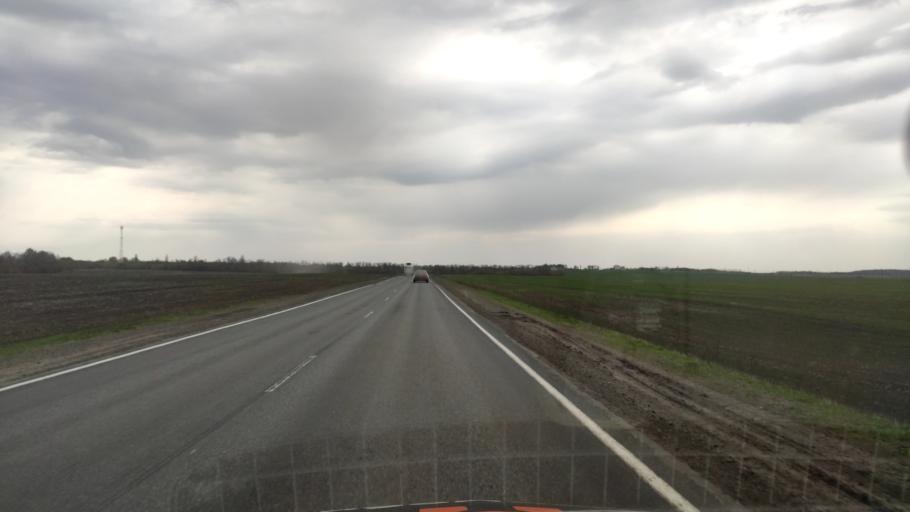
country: RU
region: Kursk
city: Gorshechnoye
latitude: 51.5481
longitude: 38.0286
